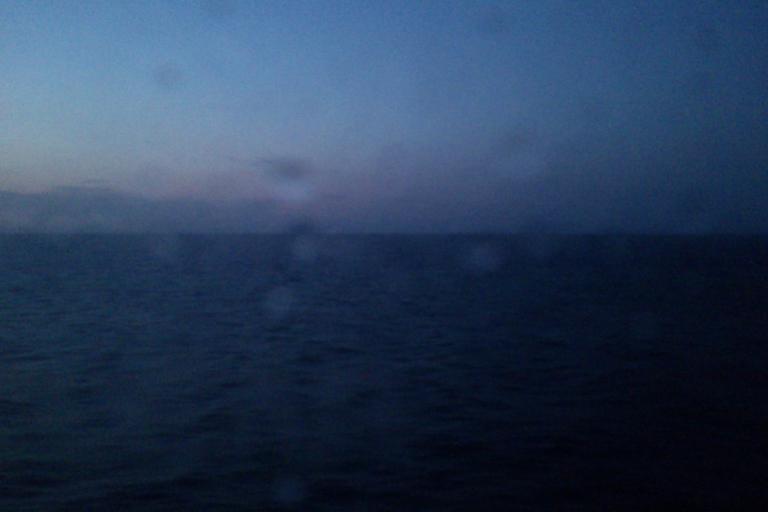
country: JP
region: Ishikawa
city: Kanazawa-shi
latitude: 37.0235
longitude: 135.9879
